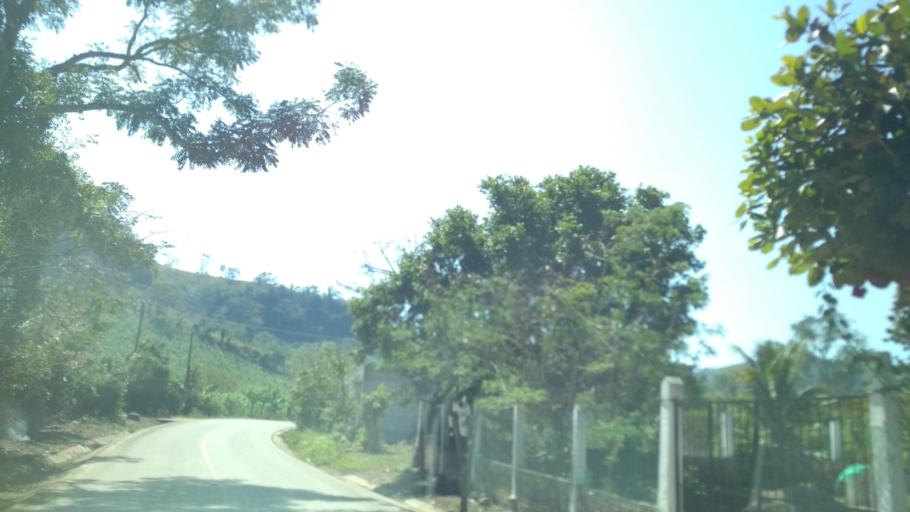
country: MX
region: Veracruz
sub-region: Papantla
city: Polutla
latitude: 20.4795
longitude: -97.2043
